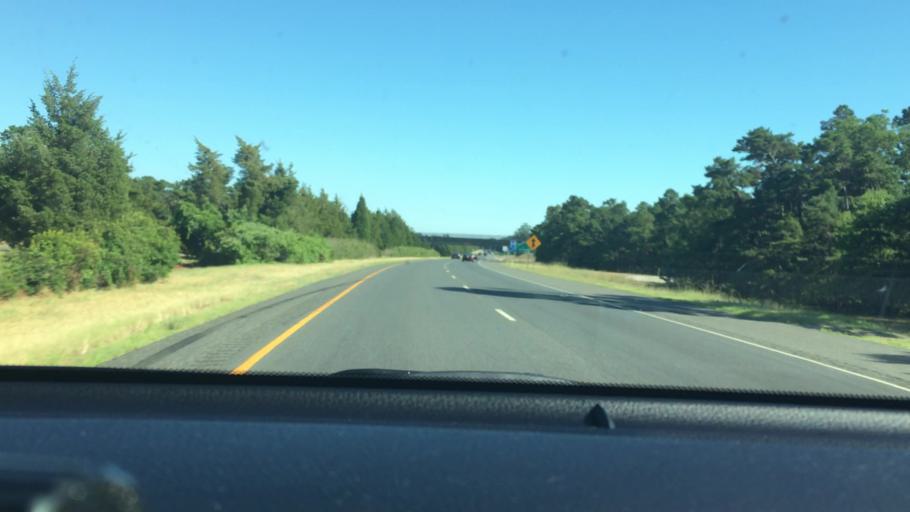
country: US
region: New Jersey
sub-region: Cumberland County
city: South Vineland
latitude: 39.4505
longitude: -75.0654
